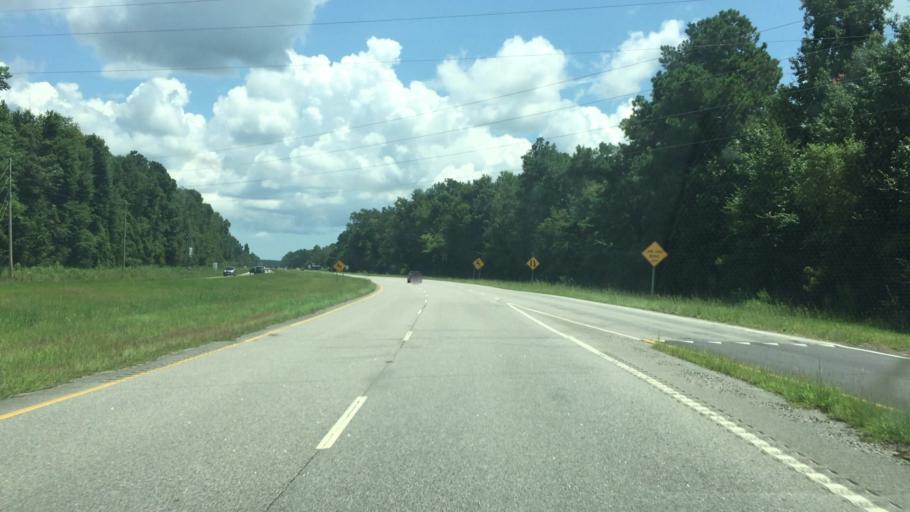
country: US
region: South Carolina
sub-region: Horry County
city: Loris
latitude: 34.0173
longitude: -78.7923
